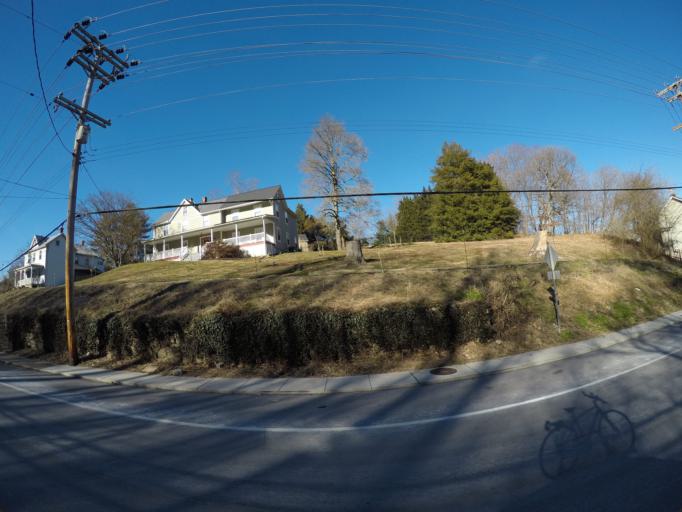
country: US
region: Maryland
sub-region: Howard County
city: Ellicott City
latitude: 39.2689
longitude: -76.8086
